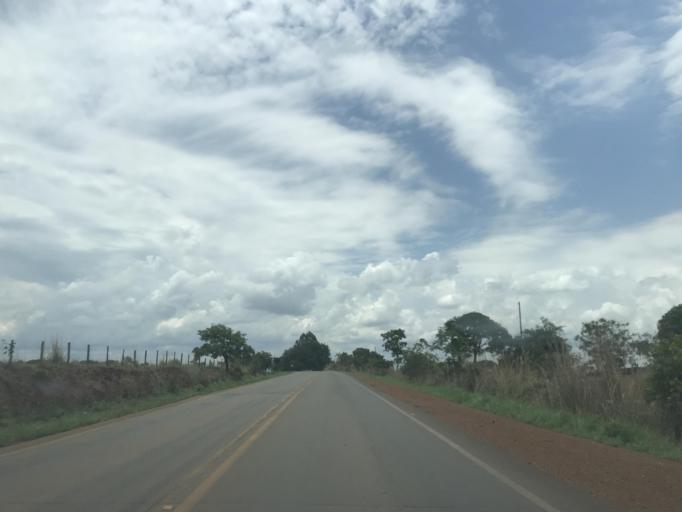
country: BR
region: Goias
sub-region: Vianopolis
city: Vianopolis
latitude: -16.7256
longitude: -48.4360
